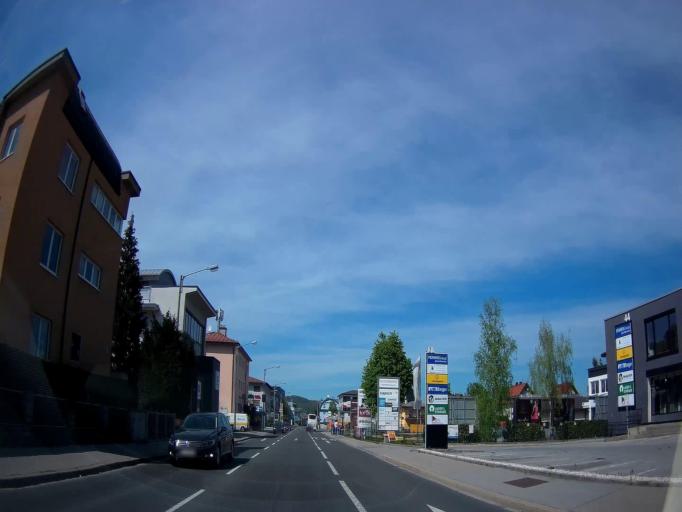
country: AT
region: Salzburg
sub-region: Salzburg Stadt
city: Salzburg
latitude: 47.8117
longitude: 13.0544
